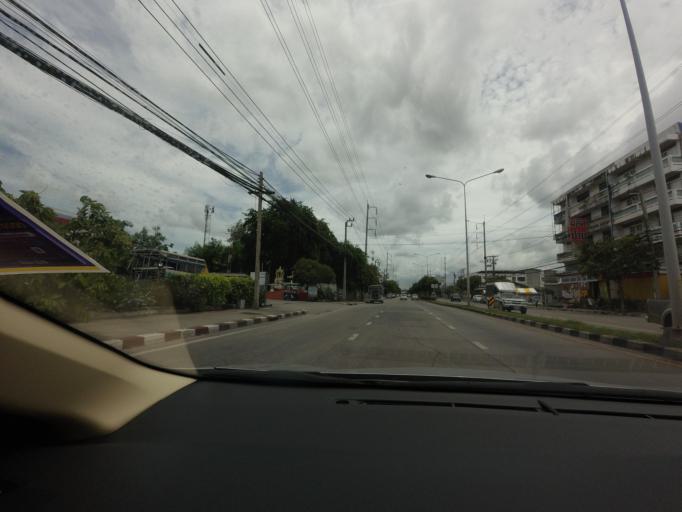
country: TH
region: Bangkok
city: Lat Krabang
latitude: 13.7183
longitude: 100.8002
